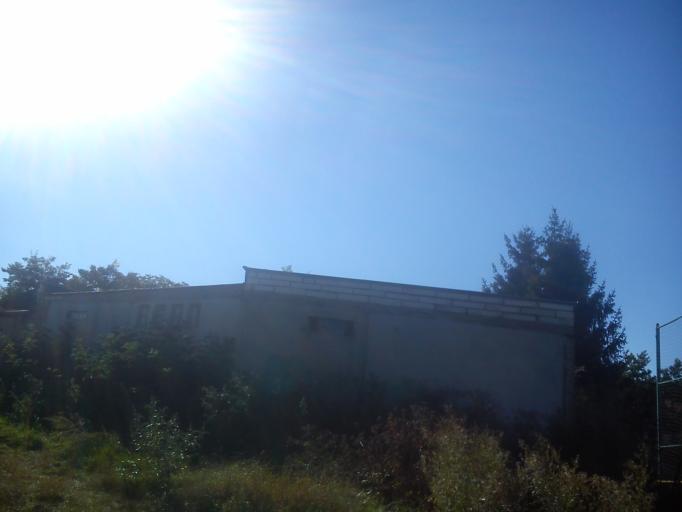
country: CZ
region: South Moravian
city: Sokolnice
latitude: 49.1024
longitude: 16.7576
